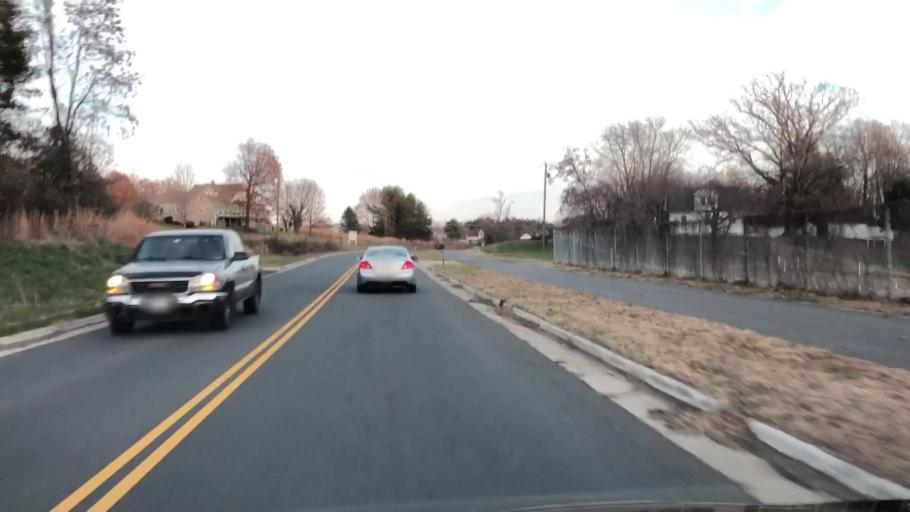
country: US
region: Virginia
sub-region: Stafford County
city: Falmouth
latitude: 38.3709
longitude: -77.4942
